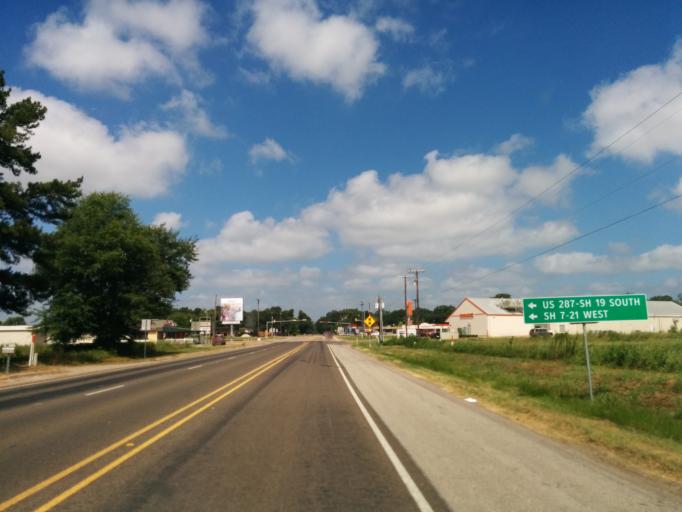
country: US
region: Texas
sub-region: Houston County
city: Crockett
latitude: 31.3147
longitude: -95.4341
